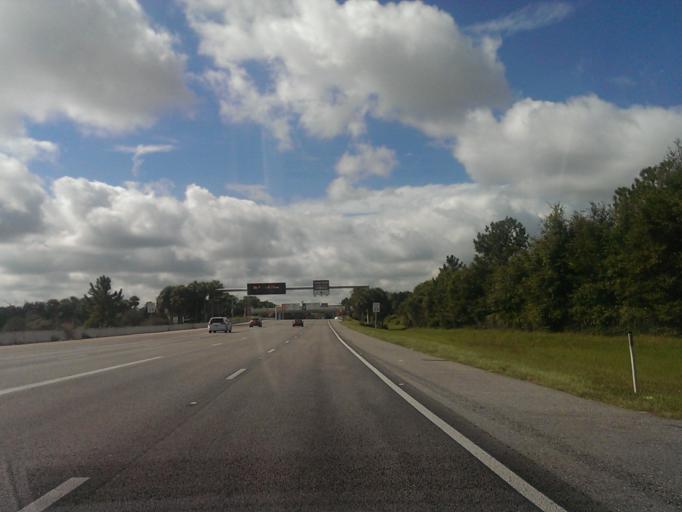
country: US
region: Florida
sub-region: Orange County
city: Belle Isle
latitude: 28.4455
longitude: -81.3097
